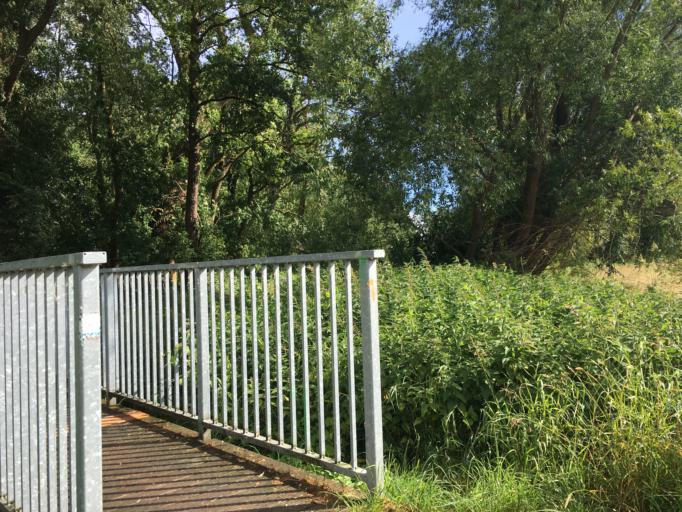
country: DE
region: Mecklenburg-Vorpommern
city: Ostseebad Boltenhagen
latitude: 53.9870
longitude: 11.1842
